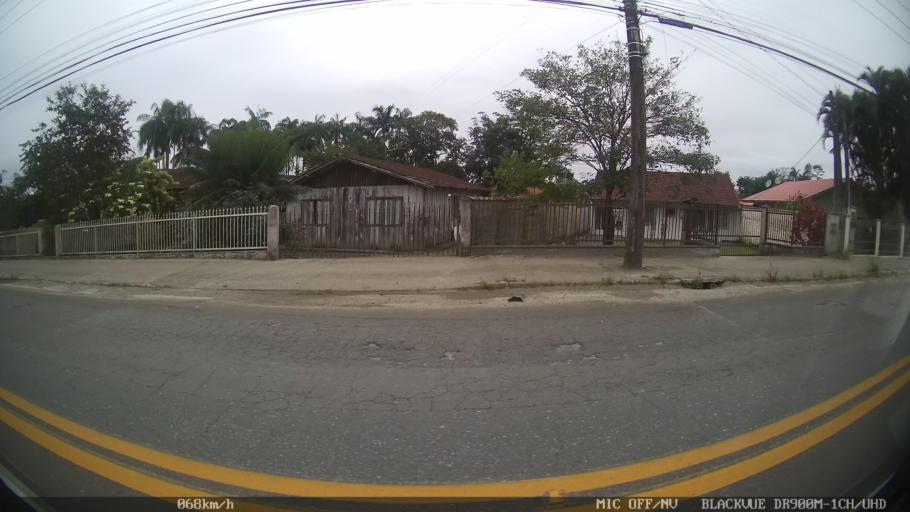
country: BR
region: Santa Catarina
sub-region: Joinville
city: Joinville
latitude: -26.2854
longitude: -48.9207
